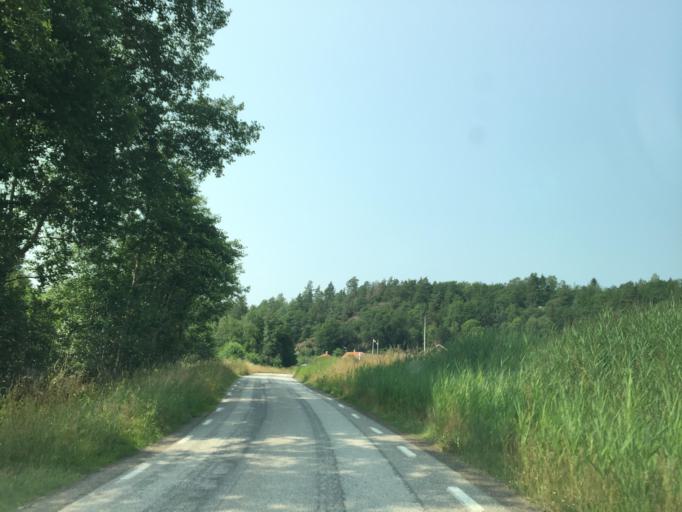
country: SE
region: Vaestra Goetaland
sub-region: Lilla Edets Kommun
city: Lilla Edet
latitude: 58.2137
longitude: 12.1345
